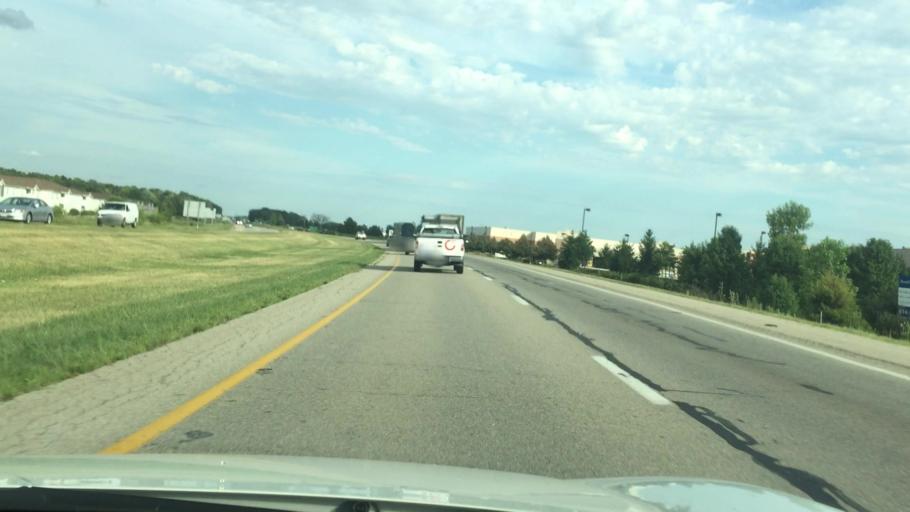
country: US
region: Ohio
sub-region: Union County
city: Marysville
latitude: 40.2327
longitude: -83.3402
